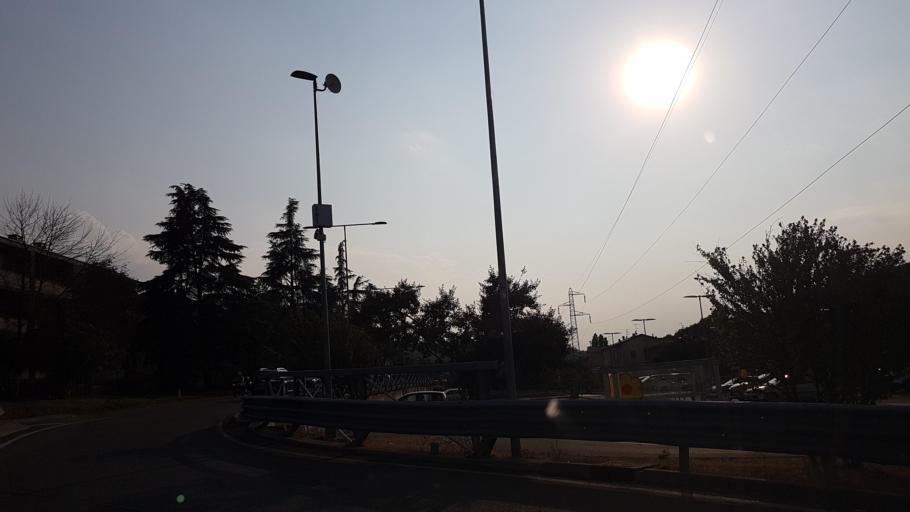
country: IT
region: Emilia-Romagna
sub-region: Provincia di Parma
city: Ricco
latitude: 44.7028
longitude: 10.1265
